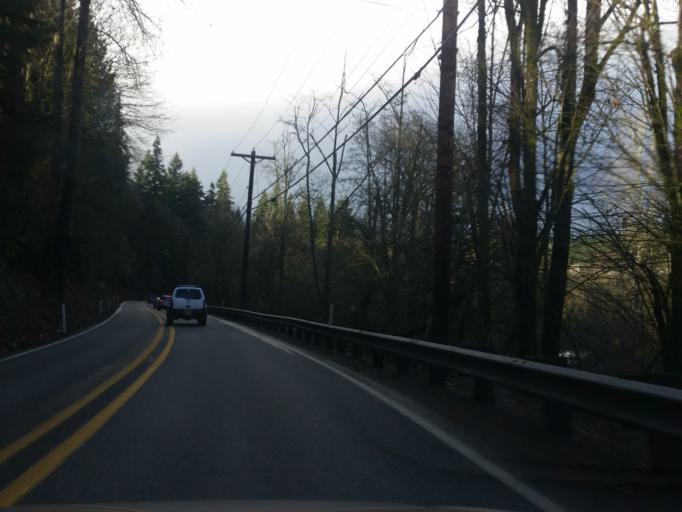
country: US
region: Washington
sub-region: Snohomish County
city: Alderwood Manor
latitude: 47.8221
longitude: -122.2566
